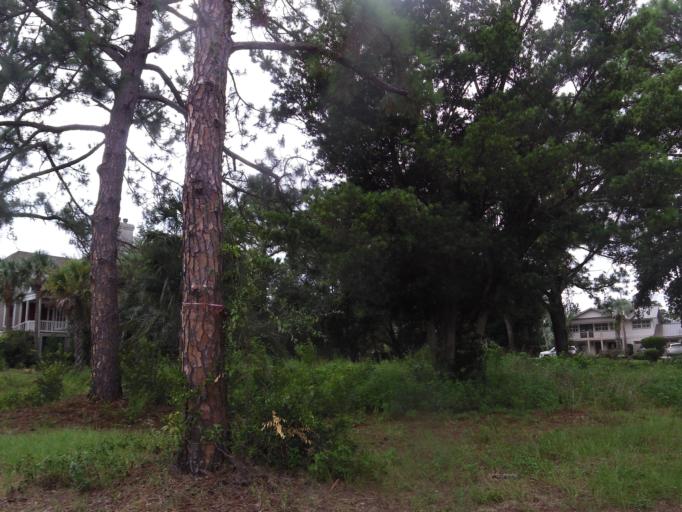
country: US
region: Georgia
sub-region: Glynn County
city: Saint Simons Island
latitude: 31.1569
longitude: -81.3671
